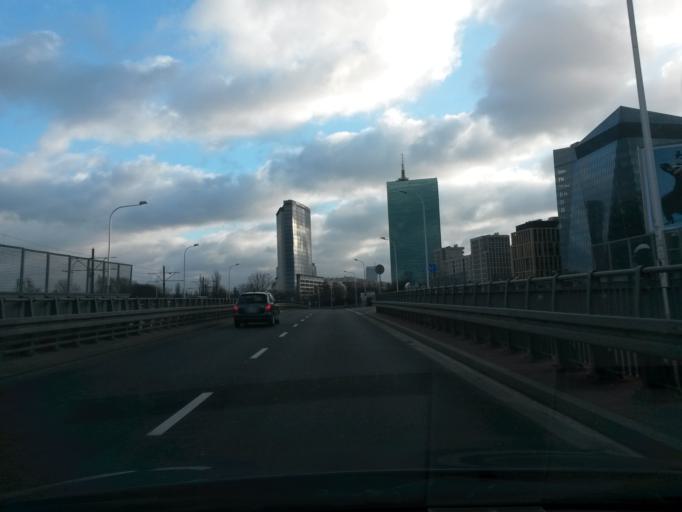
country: PL
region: Masovian Voivodeship
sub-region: Warszawa
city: Zoliborz
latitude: 52.2590
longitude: 20.9952
